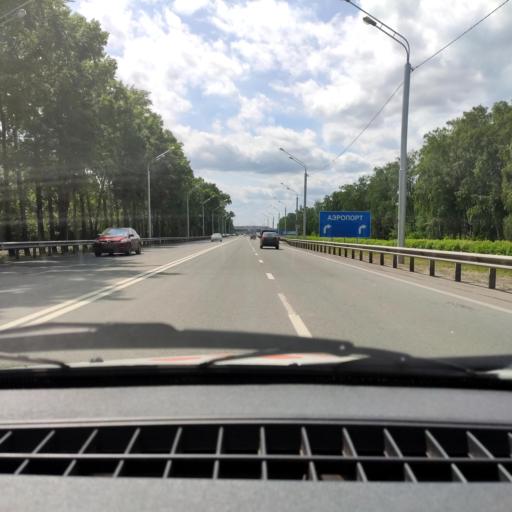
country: RU
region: Bashkortostan
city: Ufa
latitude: 54.5708
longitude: 55.8945
